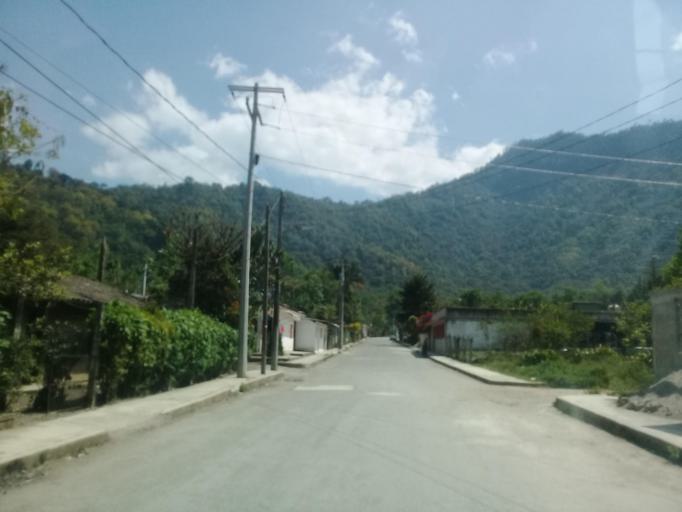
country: MX
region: Veracruz
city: Jalapilla
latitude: 18.8072
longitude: -97.0702
